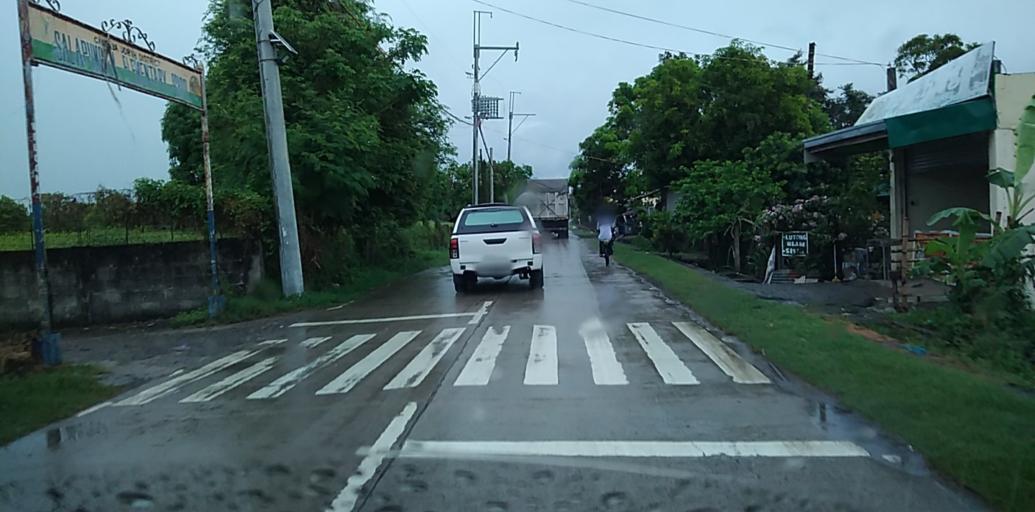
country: PH
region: Central Luzon
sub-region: Province of Pampanga
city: Salapungan
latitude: 15.1363
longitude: 120.9351
